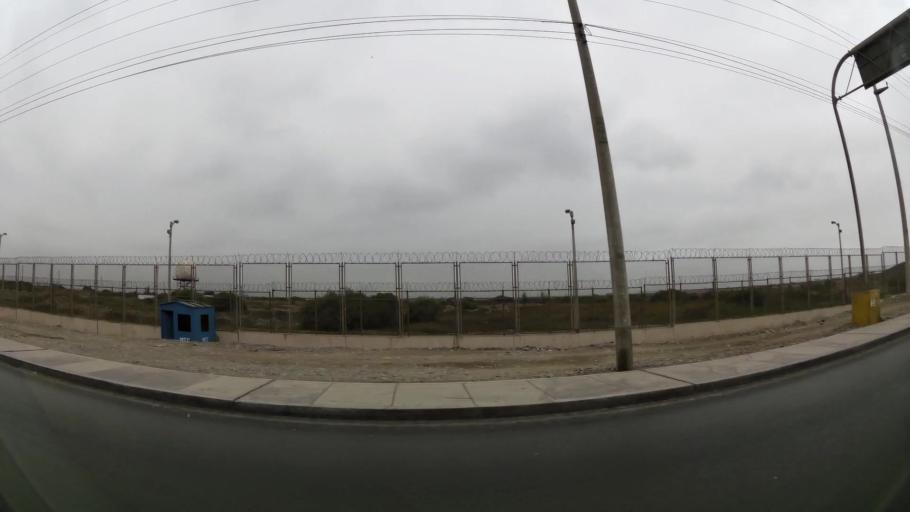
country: PE
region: Callao
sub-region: Callao
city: Callao
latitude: -12.0338
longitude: -77.1272
